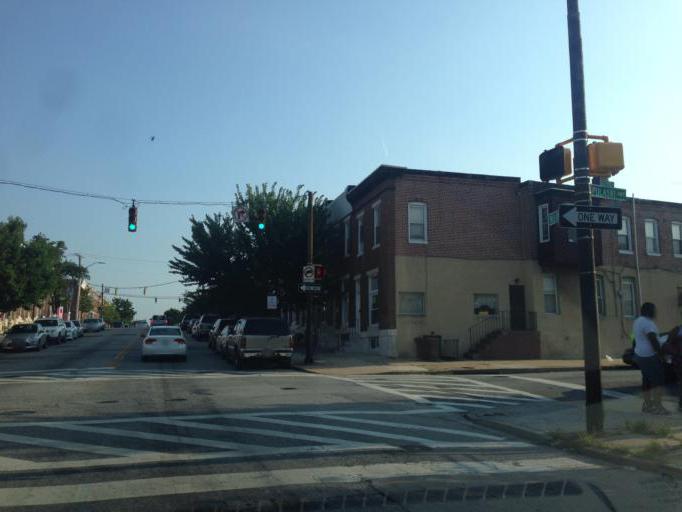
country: US
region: Maryland
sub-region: City of Baltimore
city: Baltimore
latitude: 39.2949
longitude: -76.5764
